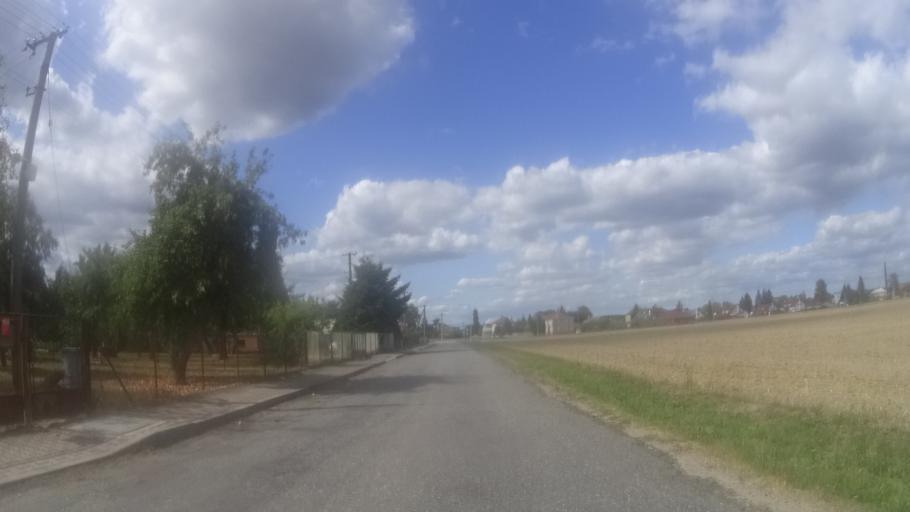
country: CZ
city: Borohradek
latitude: 50.0721
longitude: 16.1352
